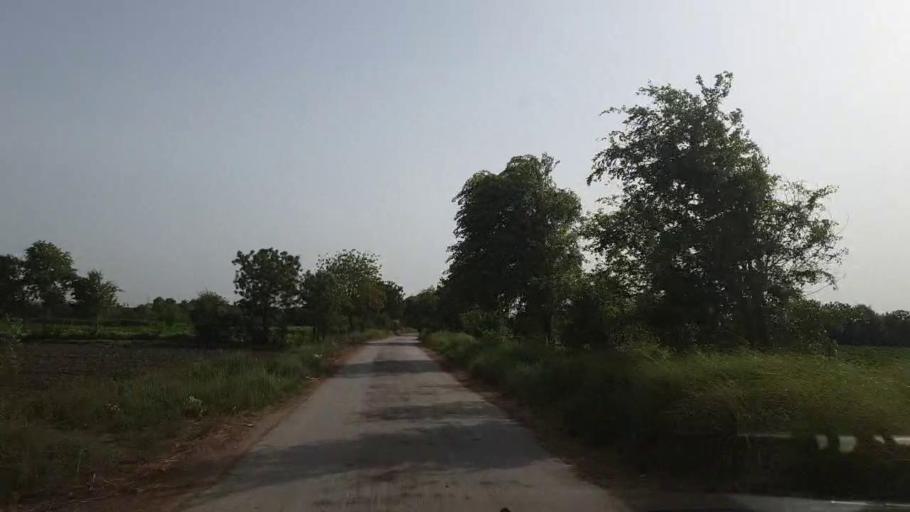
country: PK
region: Sindh
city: Nawabshah
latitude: 26.2290
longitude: 68.4059
